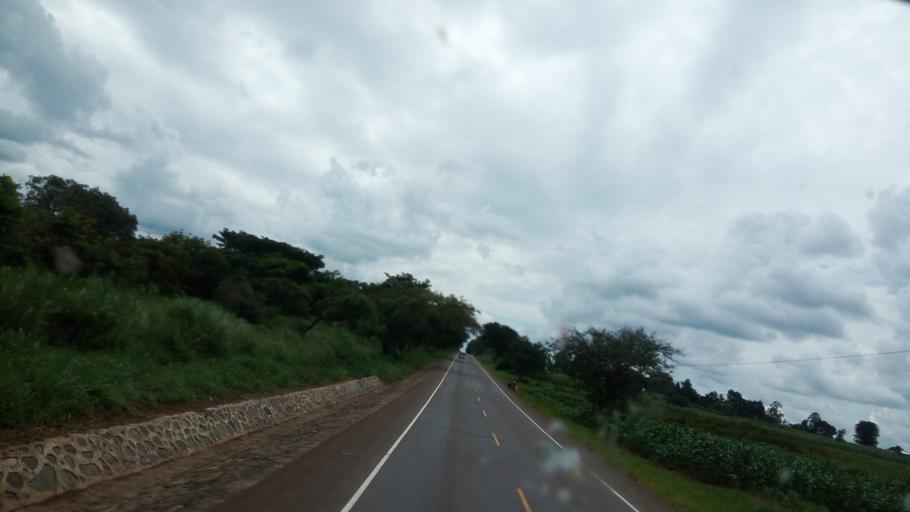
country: UG
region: Western Region
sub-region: Kiryandongo District
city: Kiryandongo
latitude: 2.0657
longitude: 32.1900
